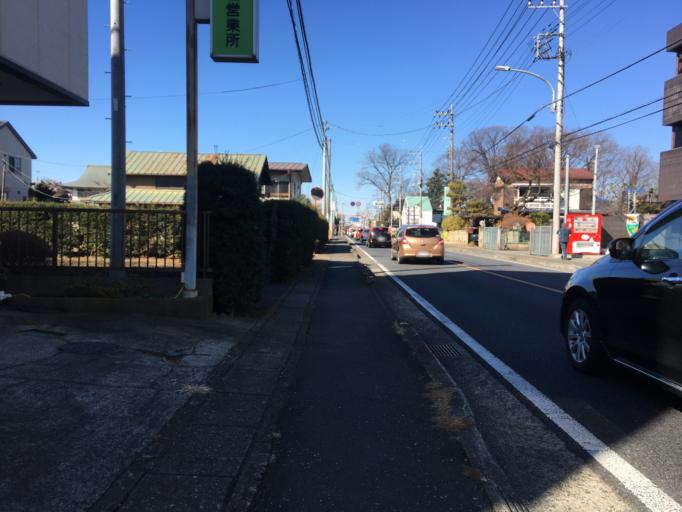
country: JP
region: Saitama
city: Oi
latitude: 35.8336
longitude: 139.5304
